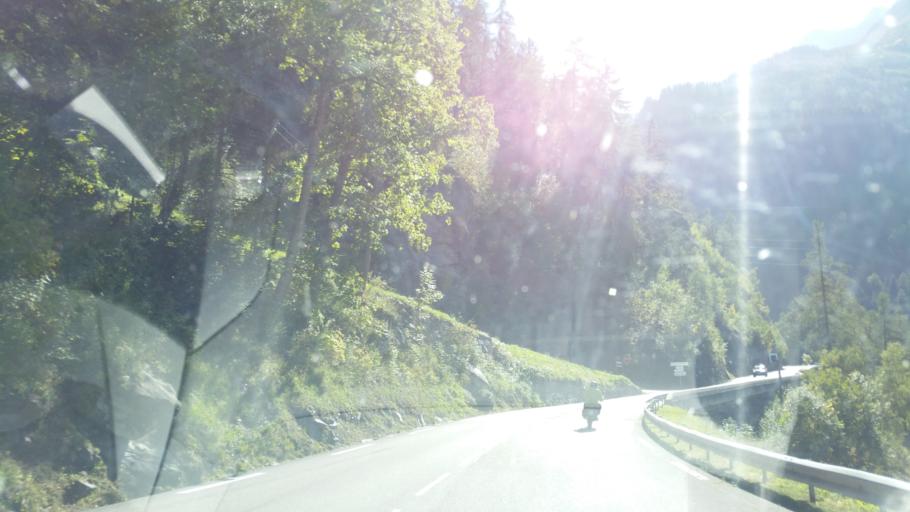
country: FR
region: Rhone-Alpes
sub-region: Departement de la Savoie
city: Tignes
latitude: 45.5798
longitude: 6.8848
